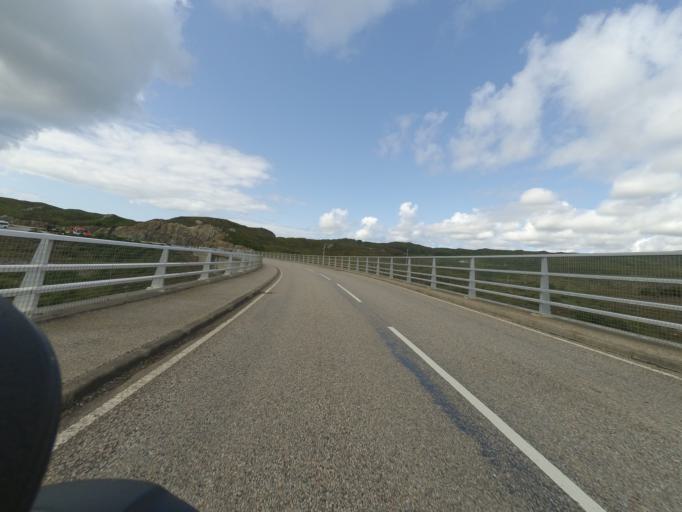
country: GB
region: Scotland
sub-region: Highland
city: Ullapool
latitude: 58.2570
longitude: -5.0236
